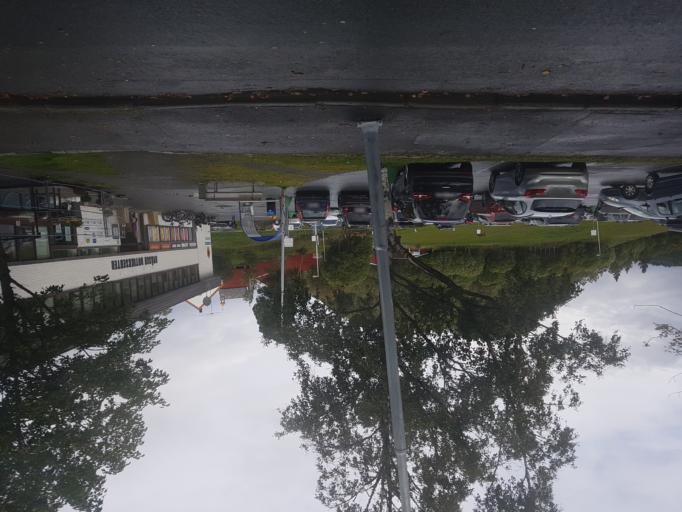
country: NO
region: Sor-Trondelag
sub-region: Trondheim
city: Trondheim
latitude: 63.4176
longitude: 10.3515
